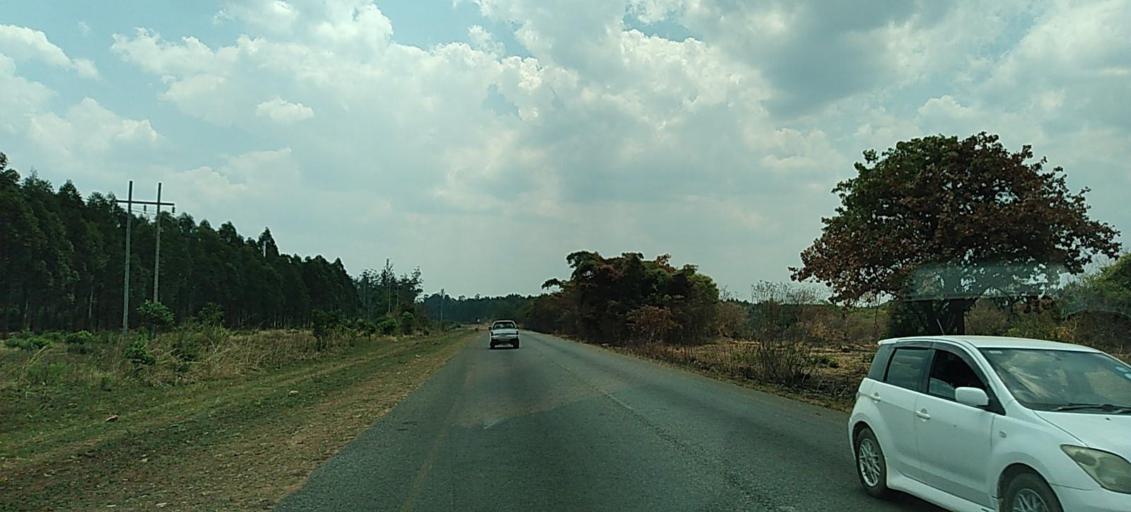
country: ZM
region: Copperbelt
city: Kalulushi
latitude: -12.8378
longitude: 27.9298
